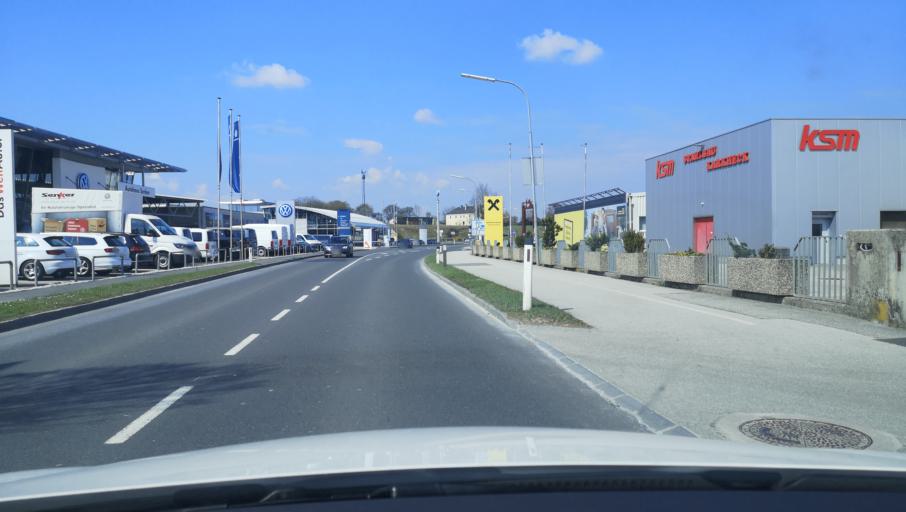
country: AT
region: Lower Austria
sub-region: Politischer Bezirk Amstetten
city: Winklarn
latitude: 48.0819
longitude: 14.8052
